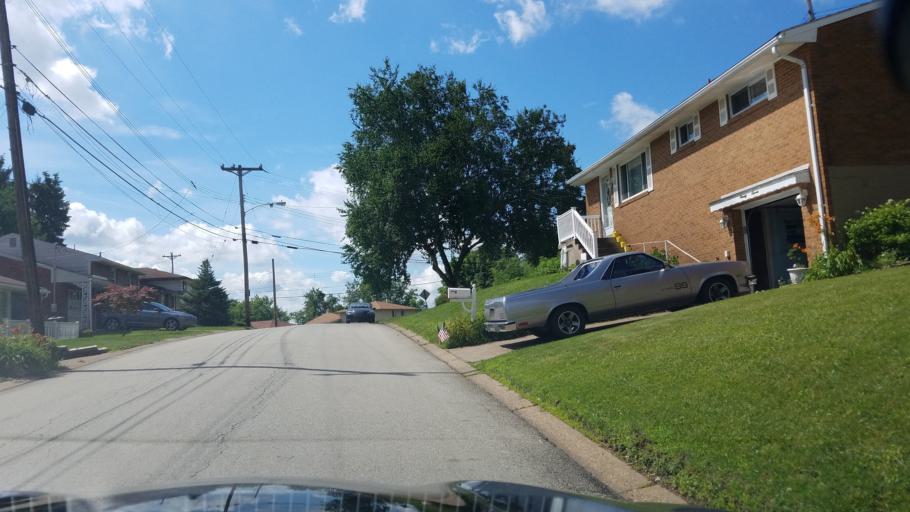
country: US
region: Pennsylvania
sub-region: Allegheny County
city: Rankin
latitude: 40.4166
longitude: -79.8730
